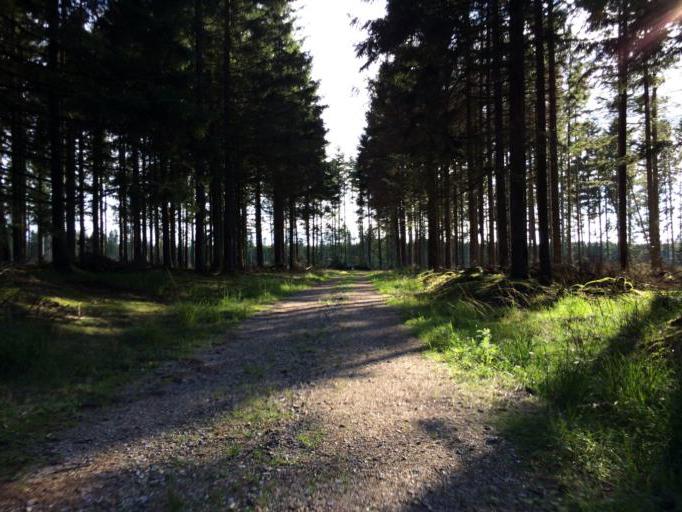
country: DK
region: Central Jutland
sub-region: Holstebro Kommune
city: Ulfborg
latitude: 56.2667
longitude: 8.4395
